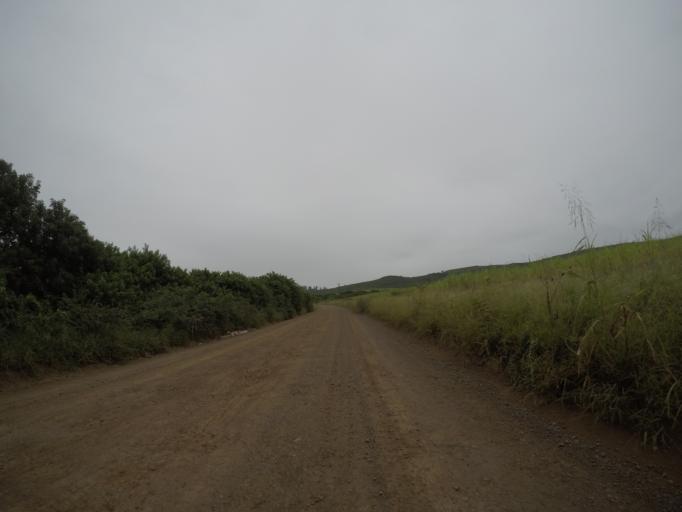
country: ZA
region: KwaZulu-Natal
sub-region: uThungulu District Municipality
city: Empangeni
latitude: -28.6573
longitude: 31.7906
